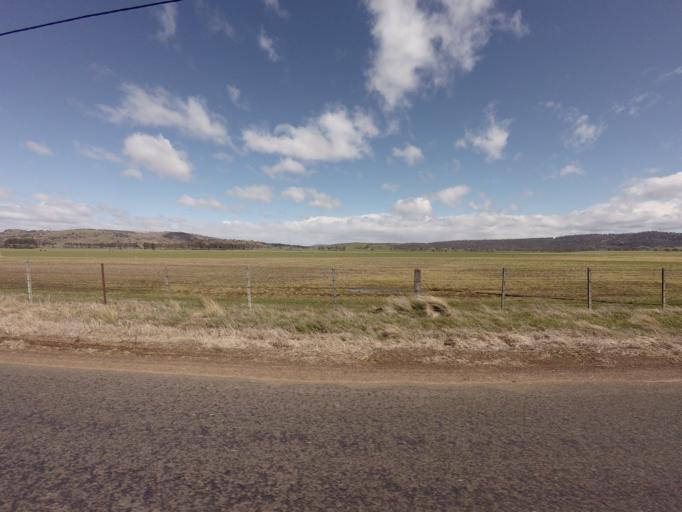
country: AU
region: Tasmania
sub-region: Northern Midlands
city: Evandale
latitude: -42.0207
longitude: 147.4696
